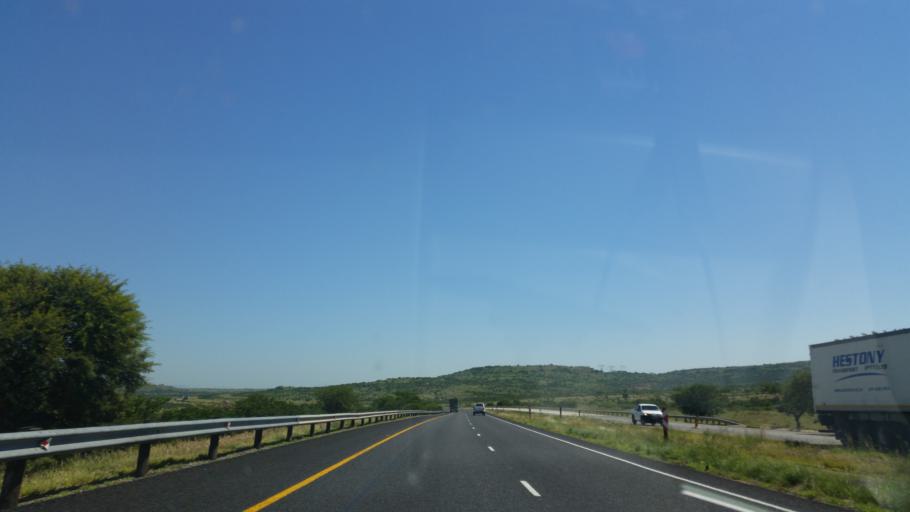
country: ZA
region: KwaZulu-Natal
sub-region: uThukela District Municipality
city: Ladysmith
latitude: -28.7019
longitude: 29.6397
